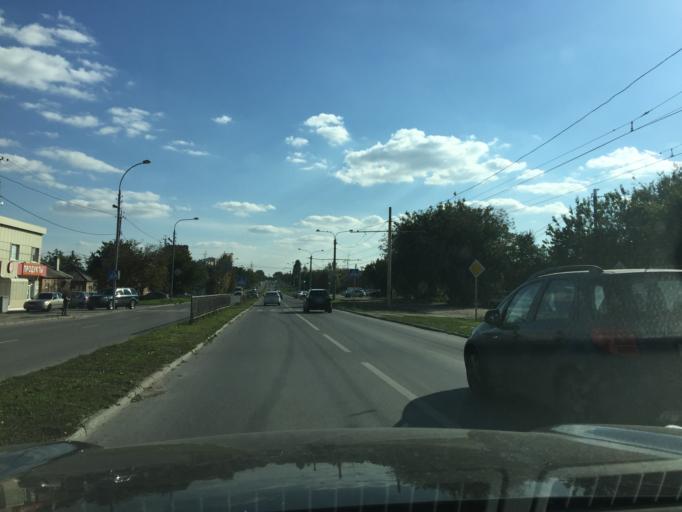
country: RU
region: Rostov
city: Rostov-na-Donu
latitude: 47.2226
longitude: 39.6437
